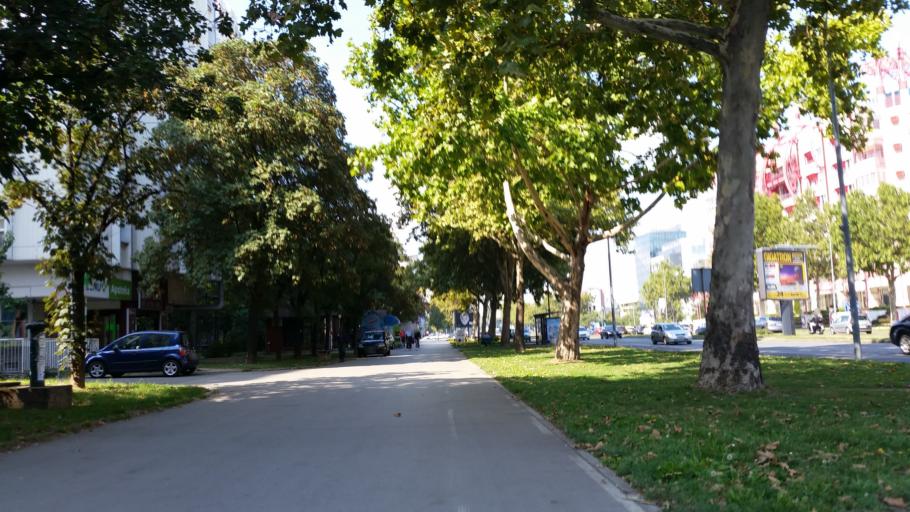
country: RS
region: Central Serbia
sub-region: Belgrade
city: Novi Beograd
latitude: 44.8213
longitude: 20.4192
